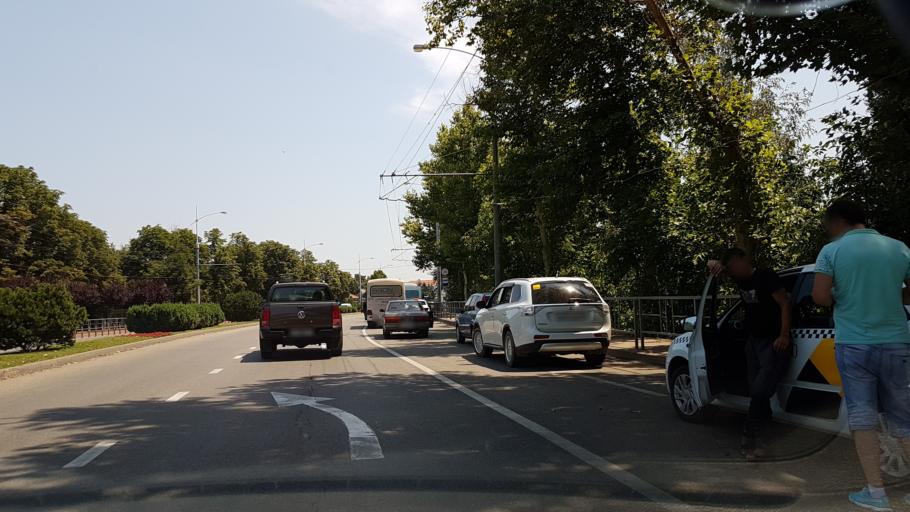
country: RU
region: Krasnodarskiy
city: Pashkovskiy
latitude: 45.0328
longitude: 39.1349
